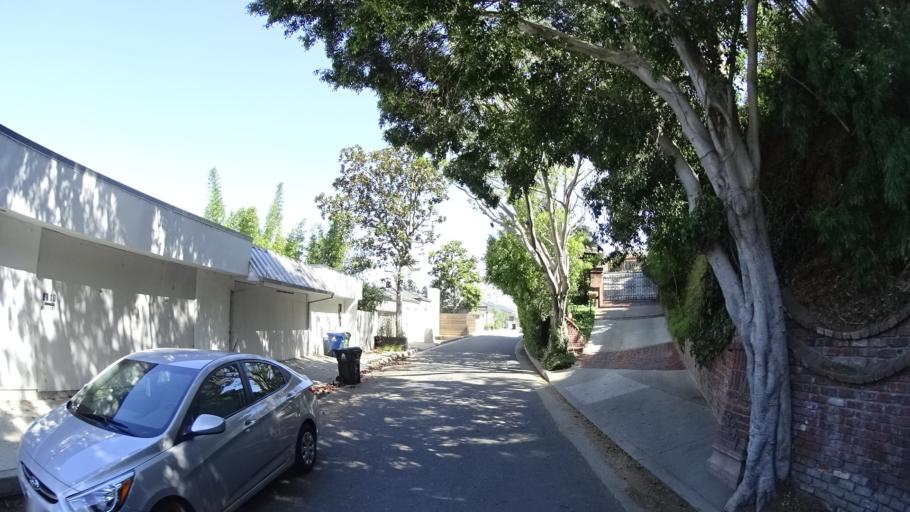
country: US
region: California
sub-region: Los Angeles County
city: West Hollywood
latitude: 34.0948
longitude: -118.3830
